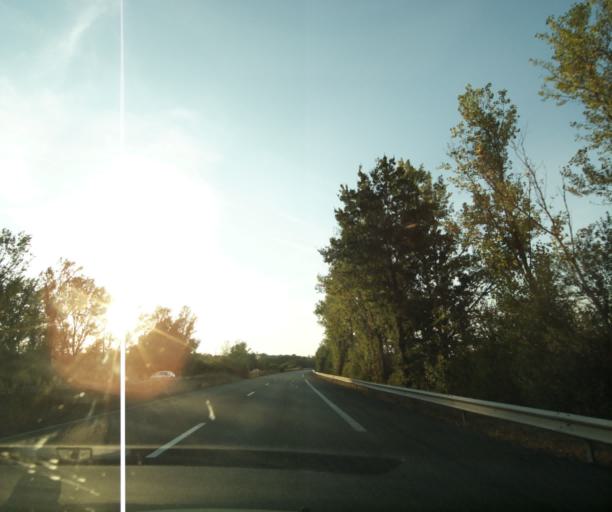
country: FR
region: Aquitaine
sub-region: Departement du Lot-et-Garonne
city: Layrac
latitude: 44.1097
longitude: 0.7370
